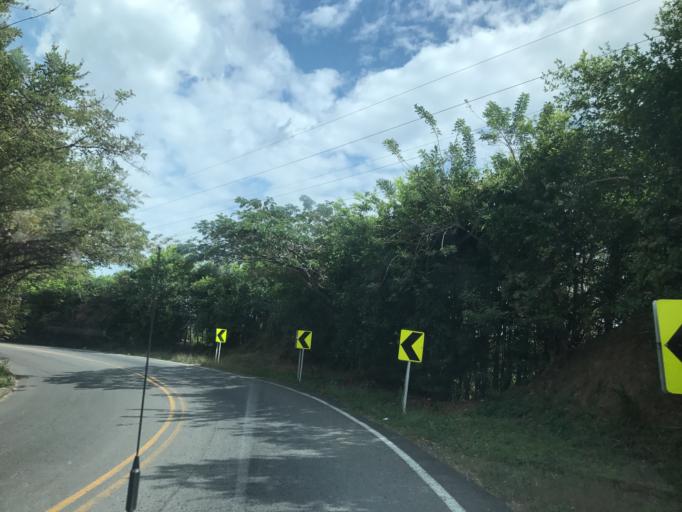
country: CO
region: Valle del Cauca
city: Cartago
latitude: 4.7279
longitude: -75.8927
